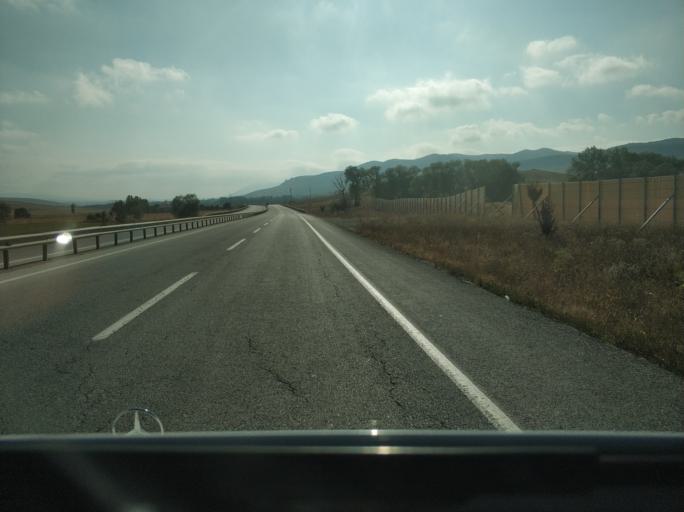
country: TR
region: Sivas
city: Yildizeli
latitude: 39.8356
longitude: 36.4398
